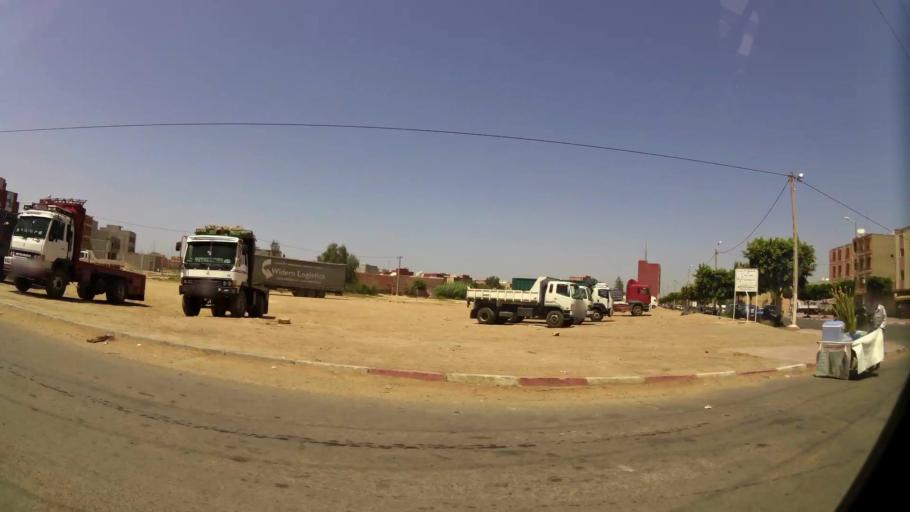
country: MA
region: Souss-Massa-Draa
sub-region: Inezgane-Ait Mellou
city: Inezgane
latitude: 30.3377
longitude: -9.4943
